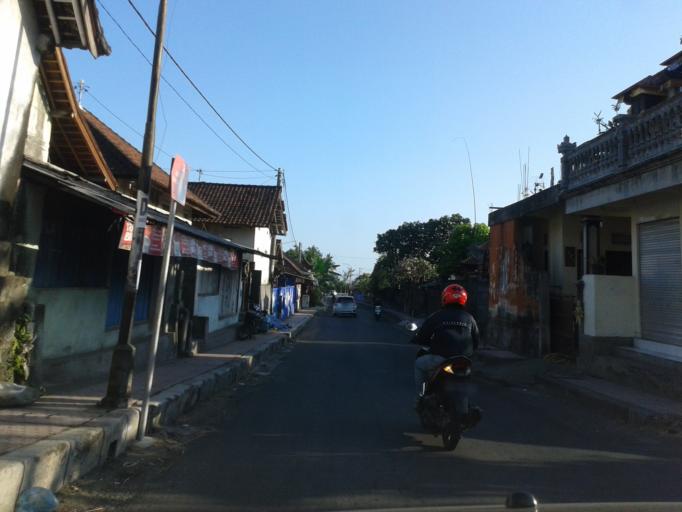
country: ID
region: Bali
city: Semarapura
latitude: -8.5662
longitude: 115.3849
